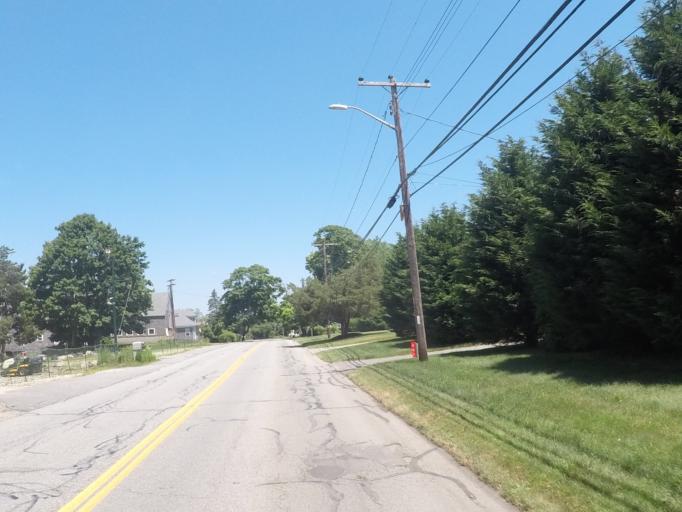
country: US
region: Massachusetts
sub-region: Bristol County
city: Bliss Corner
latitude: 41.5537
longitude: -70.9550
